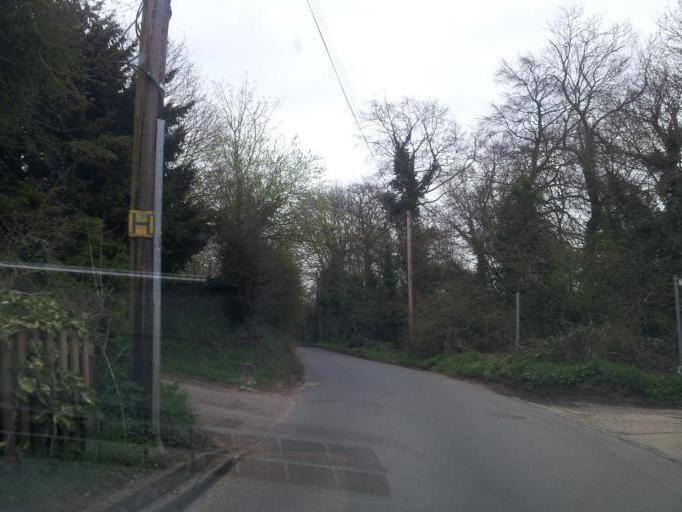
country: GB
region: England
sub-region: Hertfordshire
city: Much Hadham
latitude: 51.8803
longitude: 0.0285
